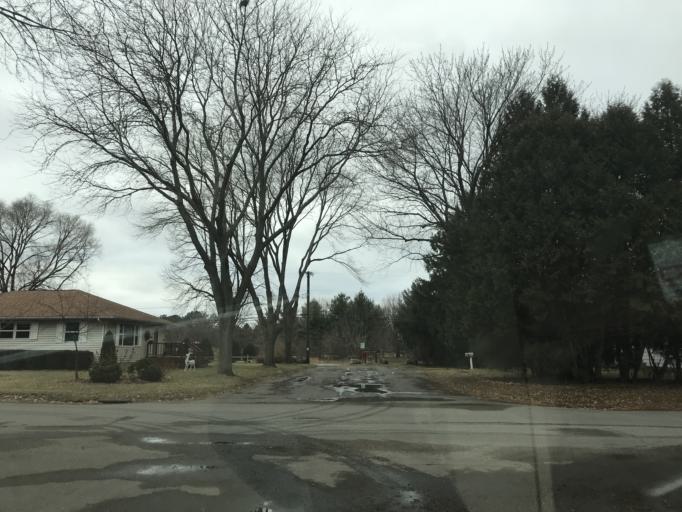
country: US
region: Wisconsin
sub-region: Dane County
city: Monona
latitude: 43.0682
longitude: -89.3154
